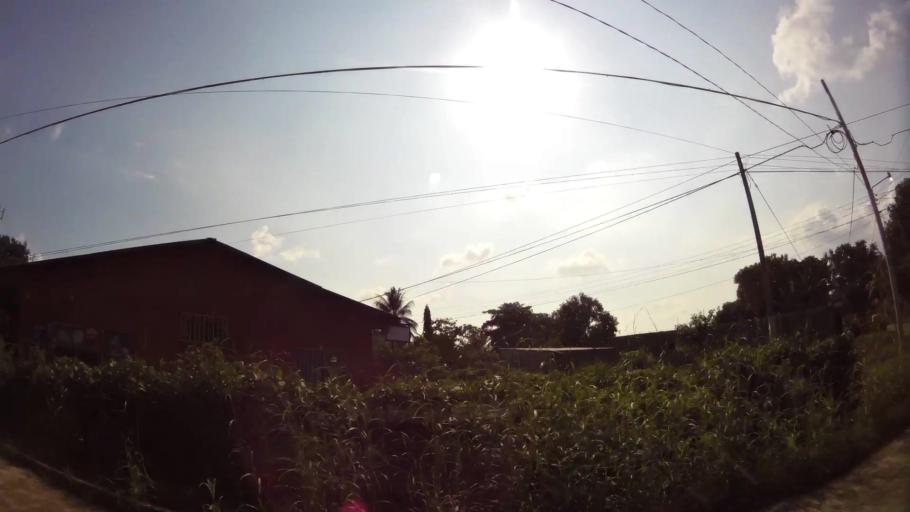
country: GT
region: Retalhuleu
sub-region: Municipio de Retalhuleu
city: Retalhuleu
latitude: 14.5395
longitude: -91.6917
